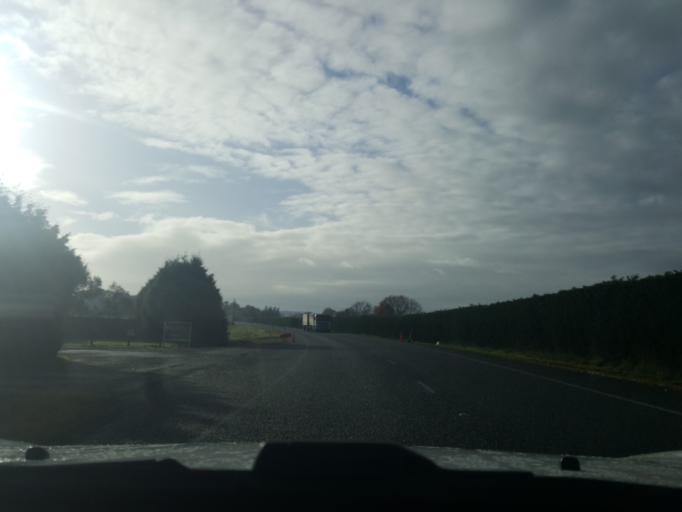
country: NZ
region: Waikato
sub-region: Waipa District
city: Cambridge
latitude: -37.7803
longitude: 175.3948
